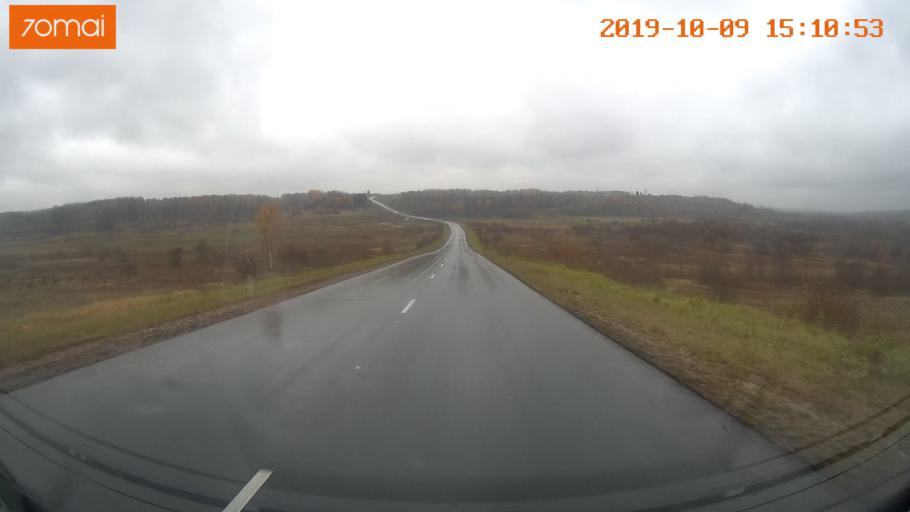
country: RU
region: Kostroma
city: Susanino
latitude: 58.1726
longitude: 41.6351
